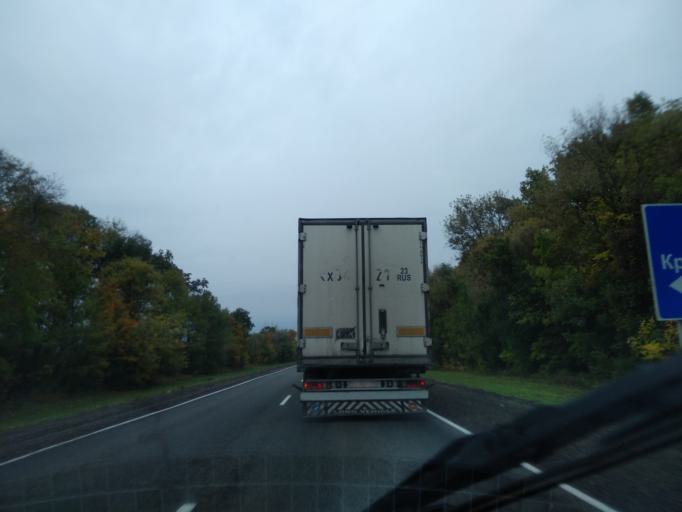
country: RU
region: Lipetsk
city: Zadonsk
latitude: 52.4556
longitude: 38.7782
